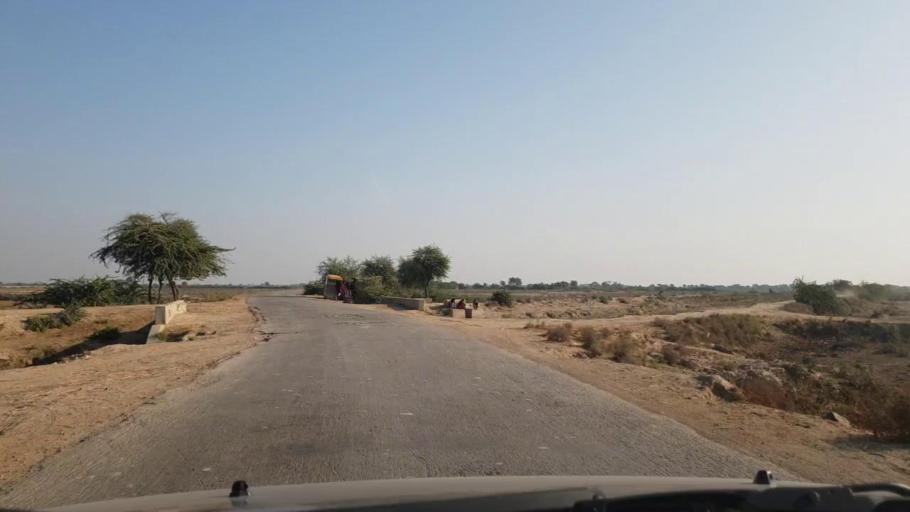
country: PK
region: Sindh
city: Tando Bago
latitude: 24.8211
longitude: 69.0067
